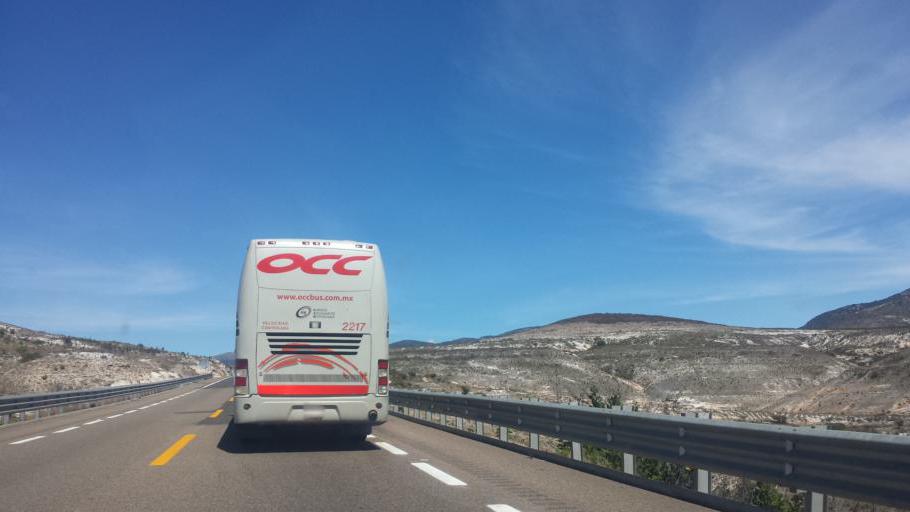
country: MX
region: Oaxaca
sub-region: Villa Tejupam de la Union
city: Villa Tejupam de la Union
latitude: 17.9022
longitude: -97.3668
